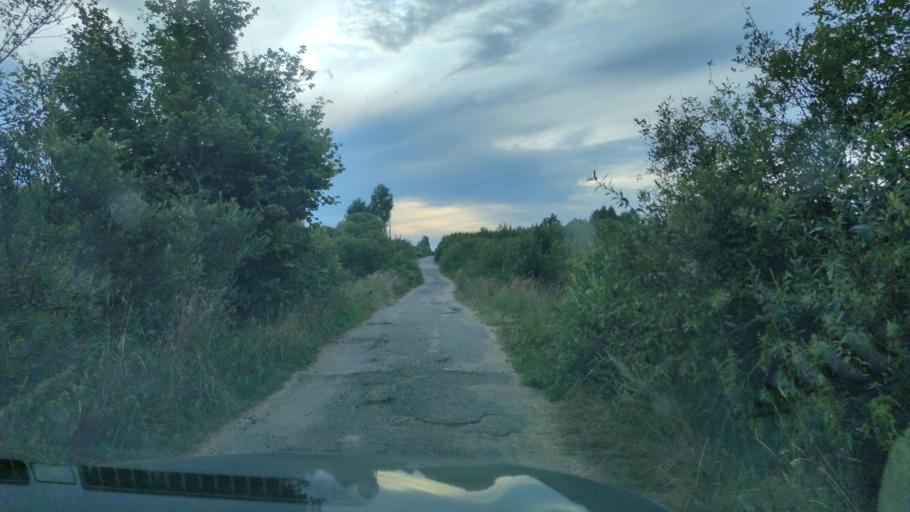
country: BY
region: Vitebsk
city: Mosar
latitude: 55.1281
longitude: 27.1619
